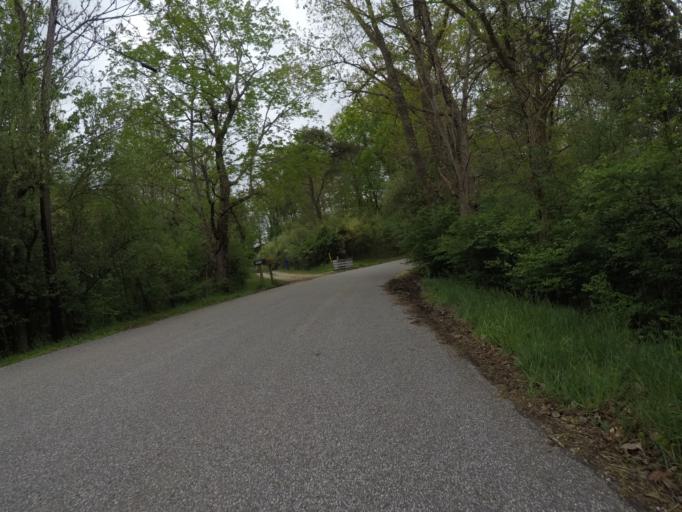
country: US
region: West Virginia
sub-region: Cabell County
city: Barboursville
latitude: 38.4019
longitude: -82.2642
